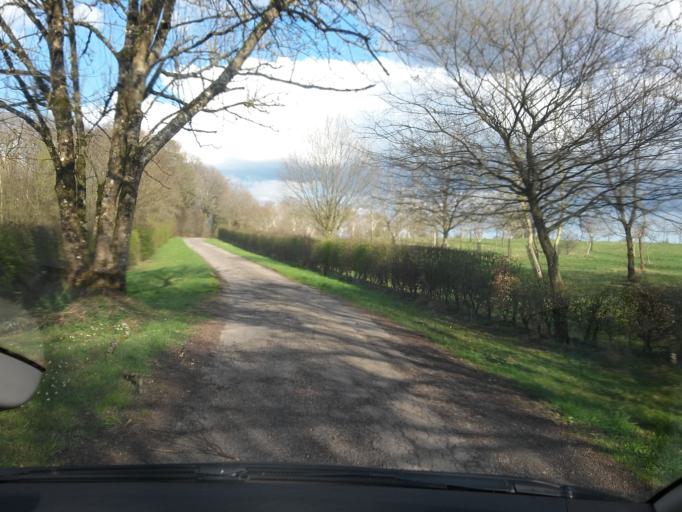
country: BE
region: Wallonia
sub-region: Province du Luxembourg
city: Florenville
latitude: 49.7232
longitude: 5.2945
